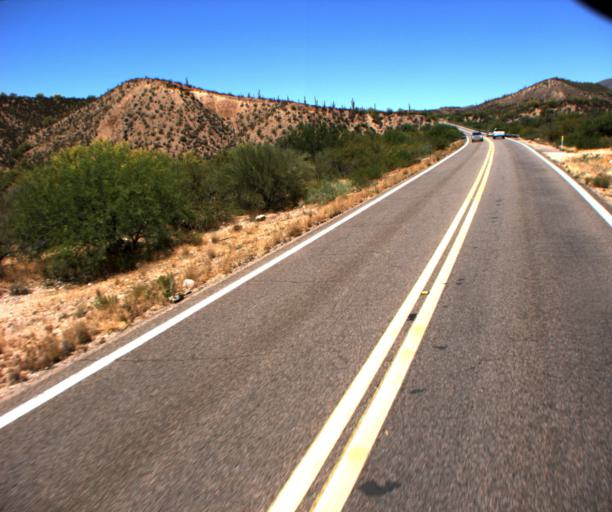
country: US
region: Arizona
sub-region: Pinal County
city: Kearny
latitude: 33.1253
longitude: -110.7751
